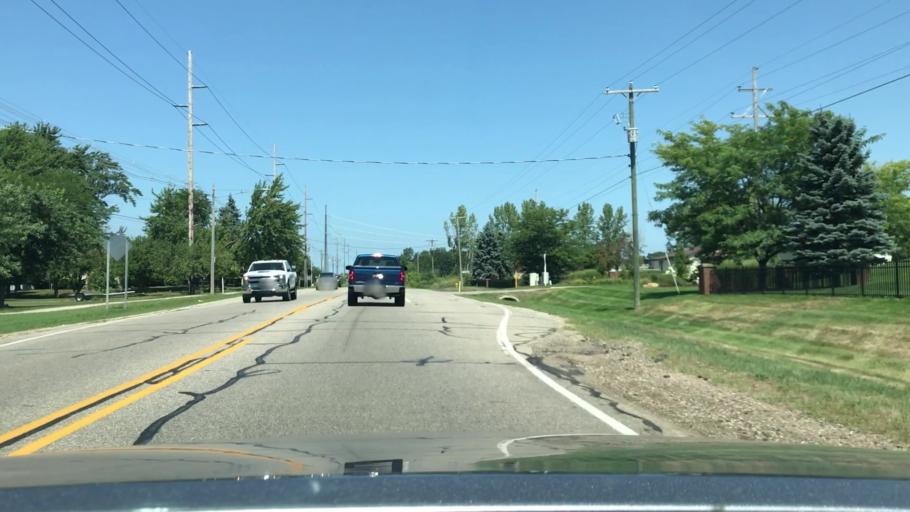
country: US
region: Michigan
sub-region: Ottawa County
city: Holland
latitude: 42.8290
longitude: -86.0783
